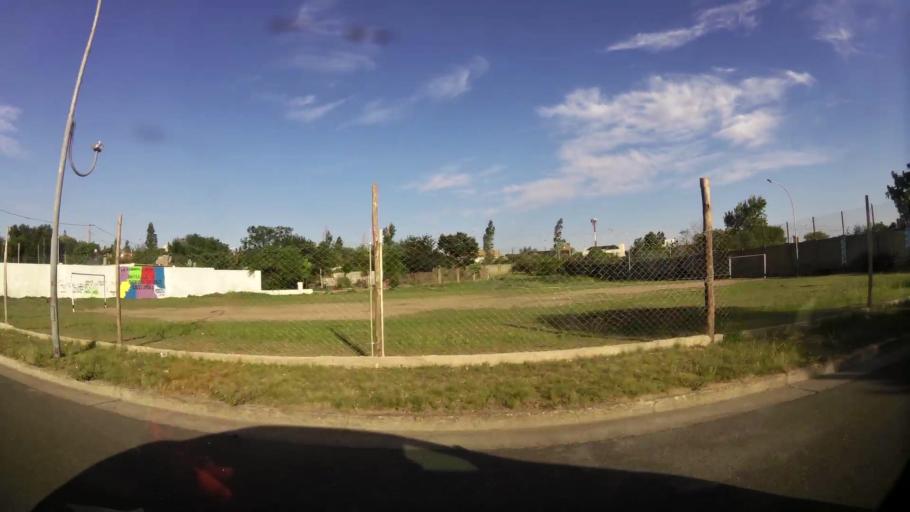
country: AR
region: Cordoba
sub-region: Departamento de Capital
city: Cordoba
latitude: -31.3809
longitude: -64.2490
